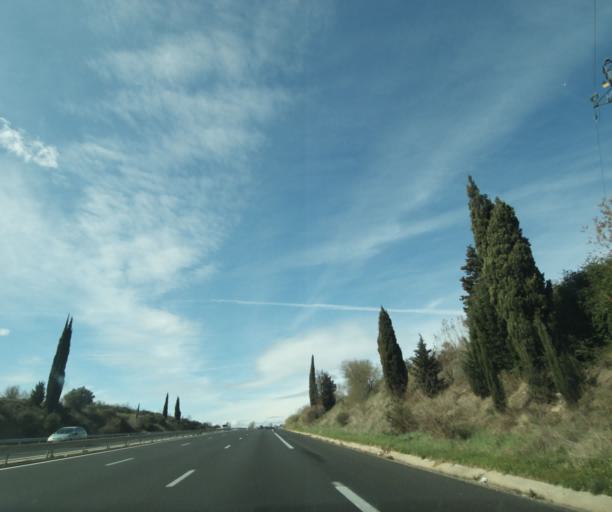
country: FR
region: Languedoc-Roussillon
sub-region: Departement du Gard
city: Sernhac
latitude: 43.9038
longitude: 4.5481
